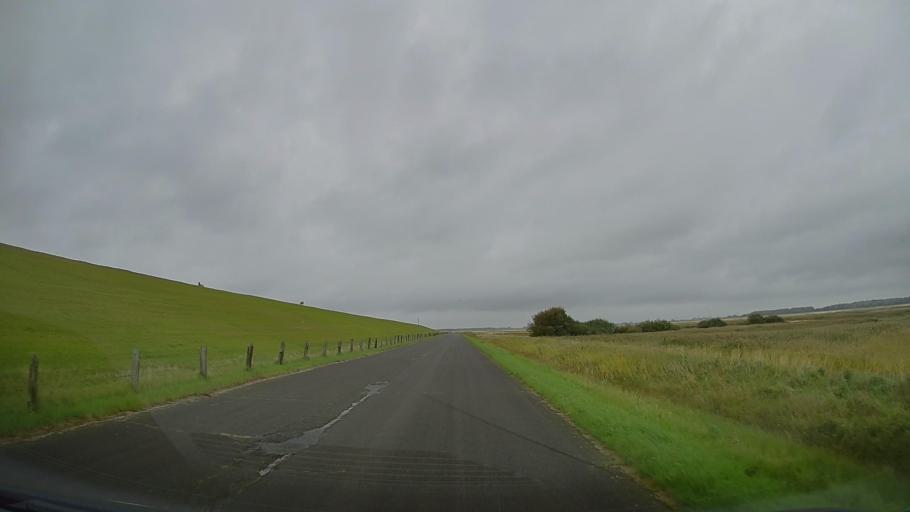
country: DE
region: Schleswig-Holstein
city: Busenwurth
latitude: 54.0517
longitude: 8.9852
